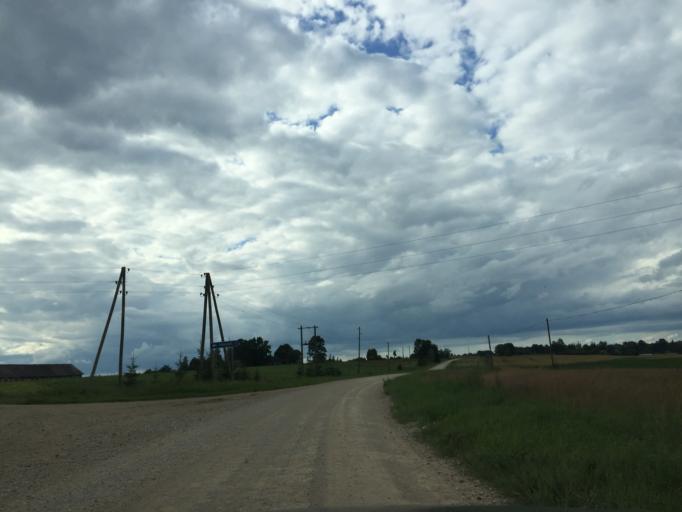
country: LV
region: Malpils
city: Malpils
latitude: 56.9660
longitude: 24.9776
